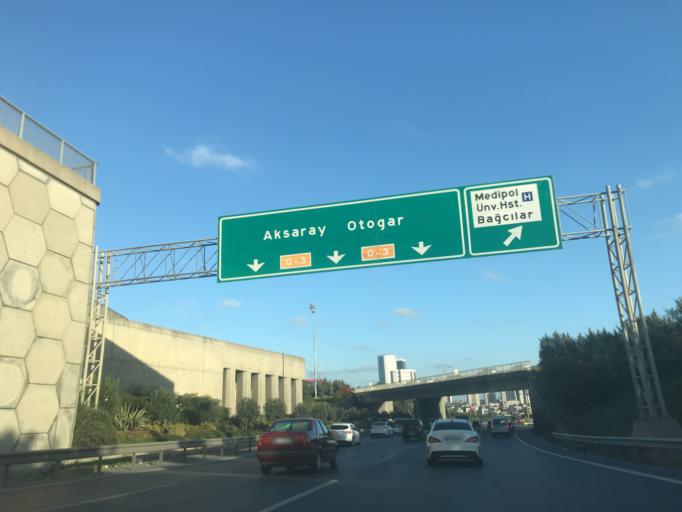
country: TR
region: Istanbul
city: Mahmutbey
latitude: 41.0616
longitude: 28.8410
